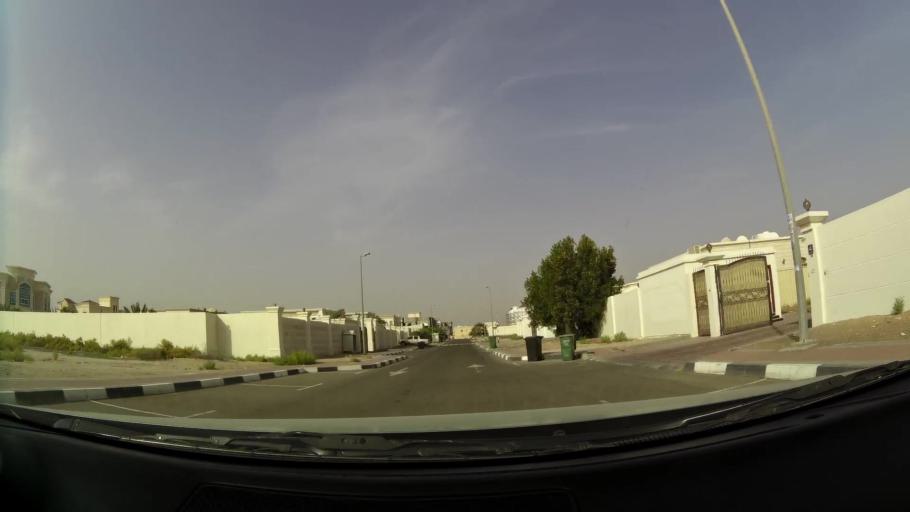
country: AE
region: Abu Dhabi
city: Al Ain
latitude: 24.1320
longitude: 55.6923
